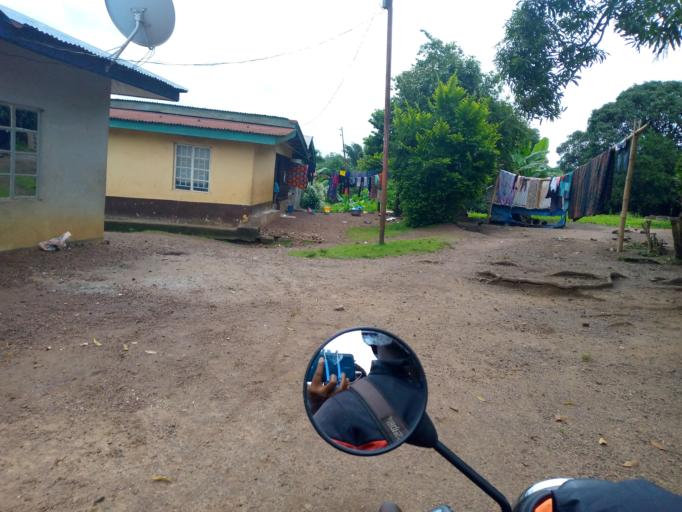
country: SL
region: Eastern Province
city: Kenema
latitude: 7.8616
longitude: -11.1914
